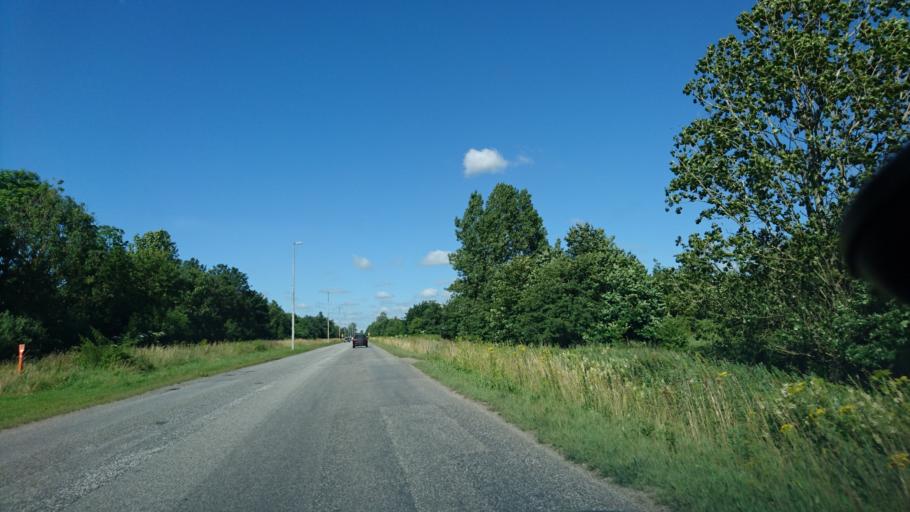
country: DK
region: North Denmark
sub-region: Alborg Kommune
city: Gistrup
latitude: 57.0254
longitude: 10.0079
